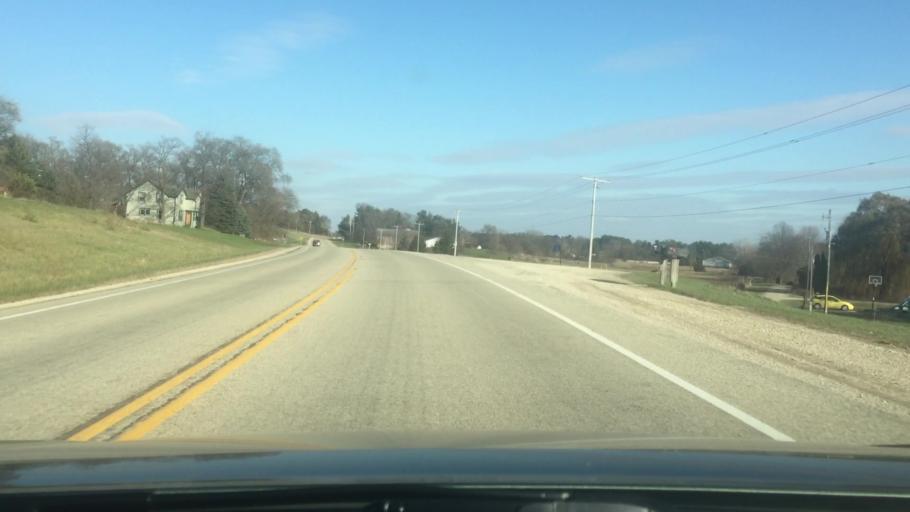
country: US
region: Wisconsin
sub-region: Jefferson County
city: Fort Atkinson
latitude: 42.9363
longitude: -88.7967
